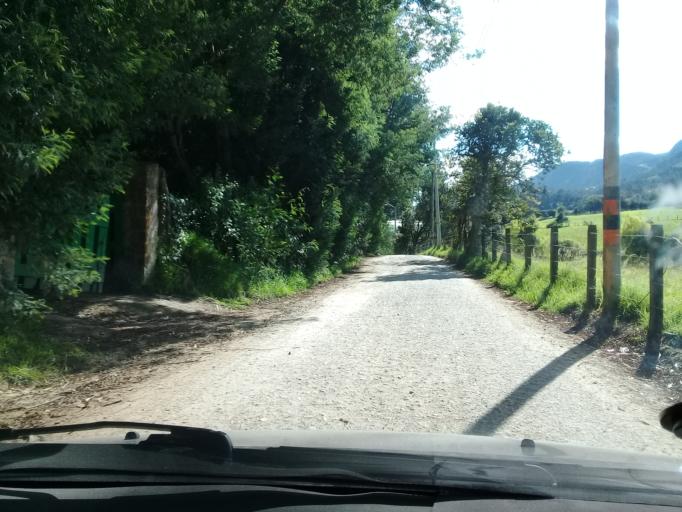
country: CO
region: Cundinamarca
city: Zipaquira
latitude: 4.9882
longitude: -74.0696
